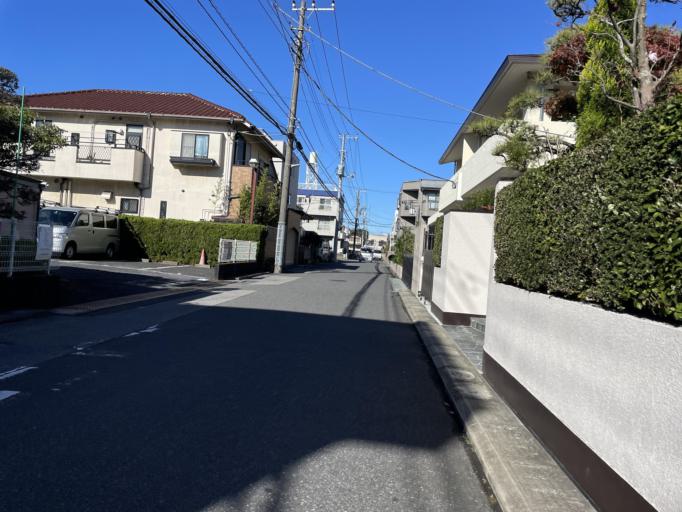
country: JP
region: Chiba
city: Nagareyama
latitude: 35.8360
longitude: 139.9034
